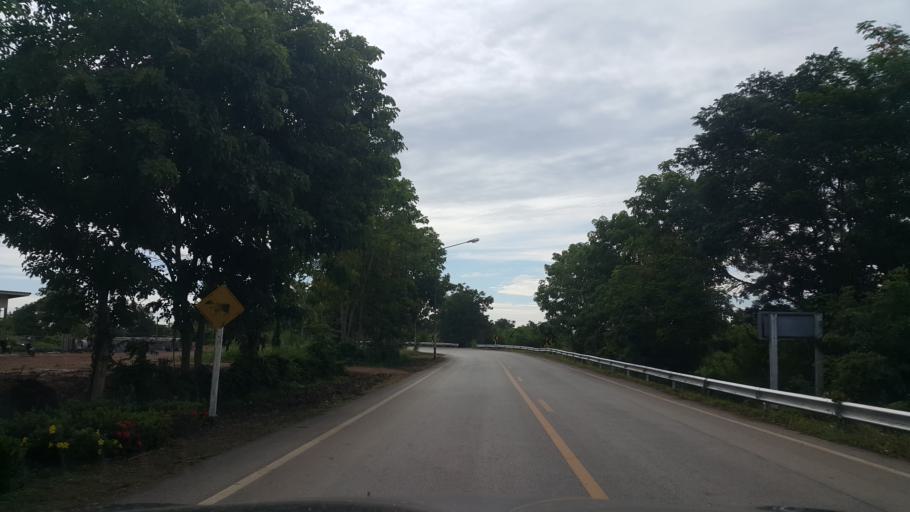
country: TH
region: Sukhothai
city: Si Nakhon
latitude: 17.2774
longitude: 99.9719
